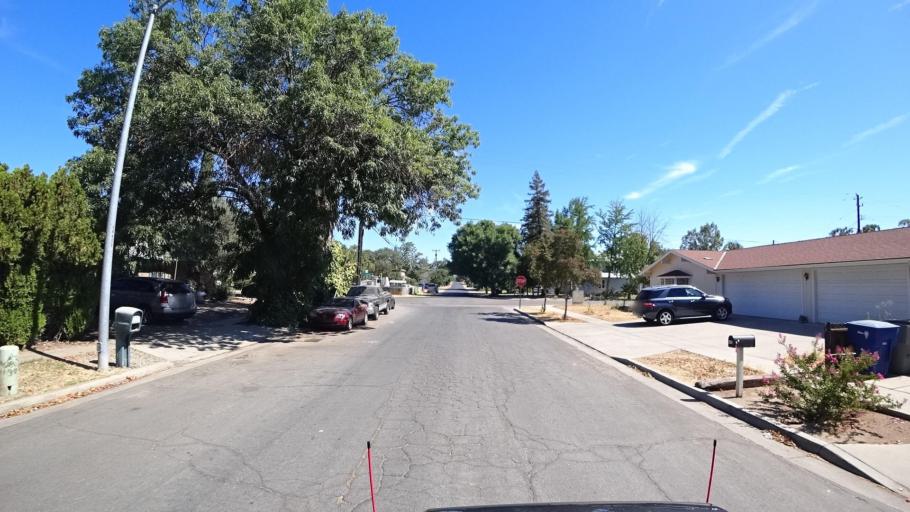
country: US
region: California
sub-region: Fresno County
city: Sunnyside
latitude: 36.7391
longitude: -119.7138
